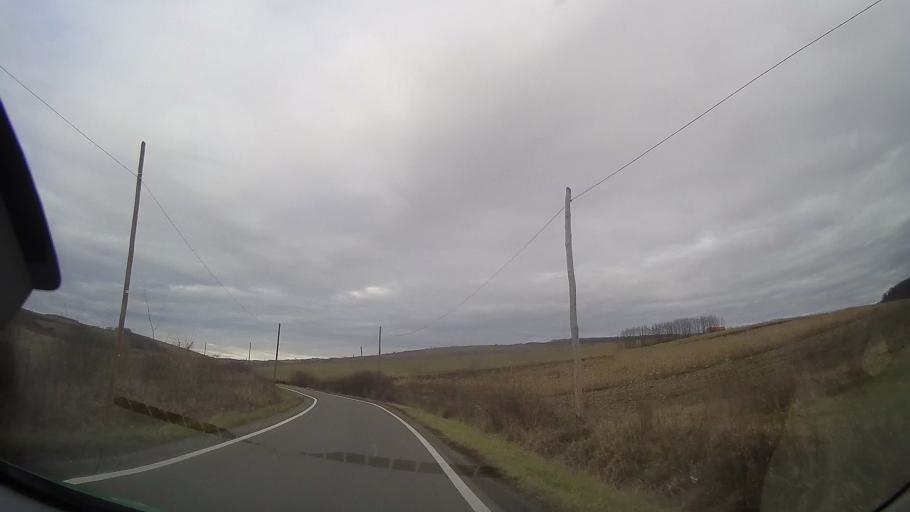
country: RO
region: Mures
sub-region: Comuna Cozma
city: Cozma
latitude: 46.7889
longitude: 24.5464
